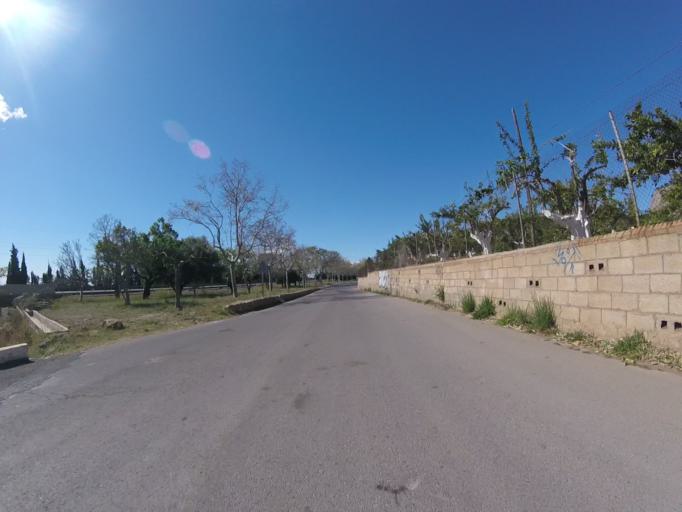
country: ES
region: Valencia
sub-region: Provincia de Castello
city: Benicassim
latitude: 40.0619
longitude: 0.0708
